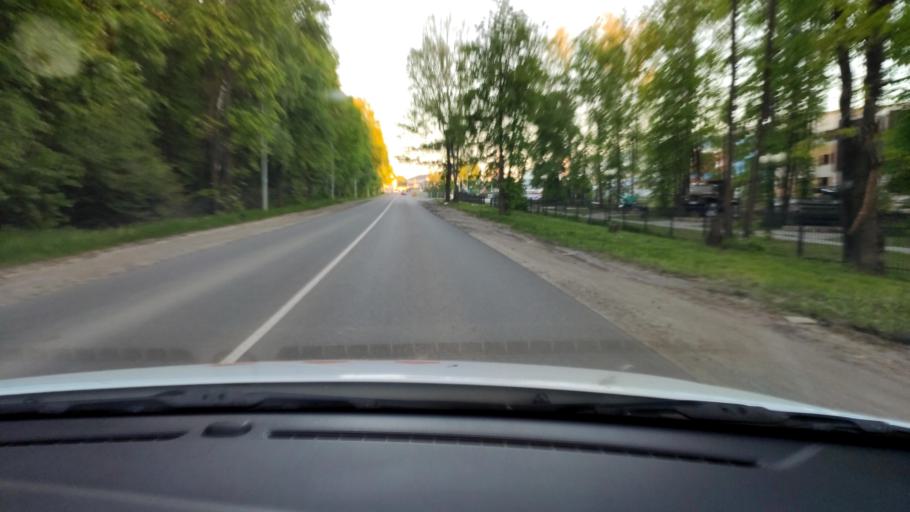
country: RU
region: Tatarstan
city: Vysokaya Gora
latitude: 55.9255
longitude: 49.3035
